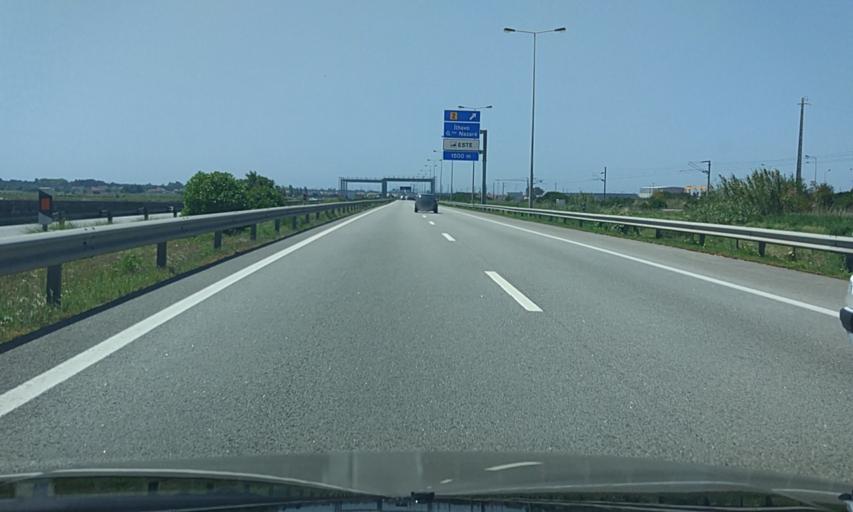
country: PT
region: Aveiro
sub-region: Aveiro
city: Aveiro
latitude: 40.6355
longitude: -8.6718
